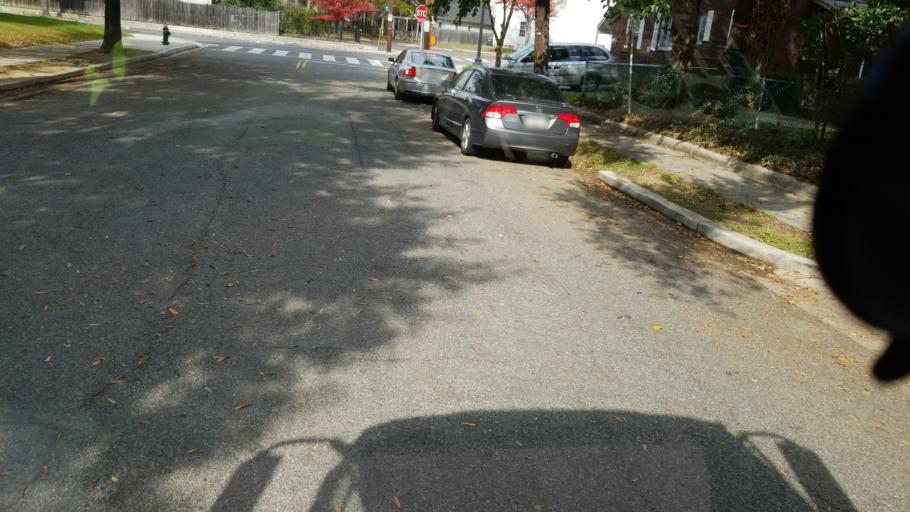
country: US
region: Maryland
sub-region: Prince George's County
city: Fairmount Heights
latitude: 38.8979
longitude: -76.9192
